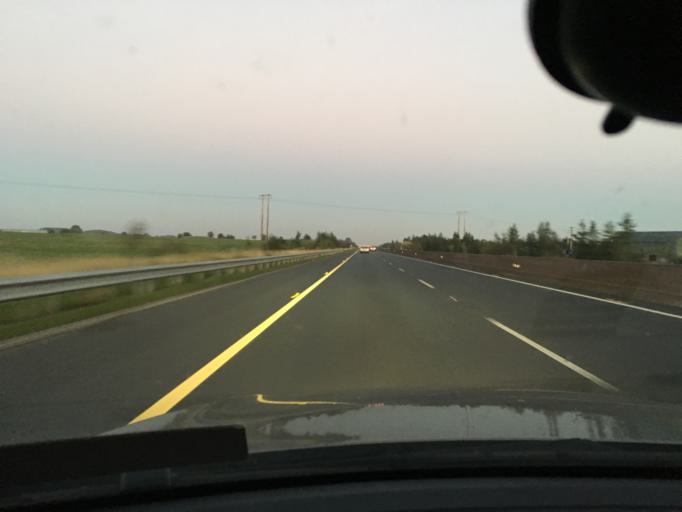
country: IE
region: Connaught
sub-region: County Galway
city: Athenry
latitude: 53.2757
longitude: -8.7145
